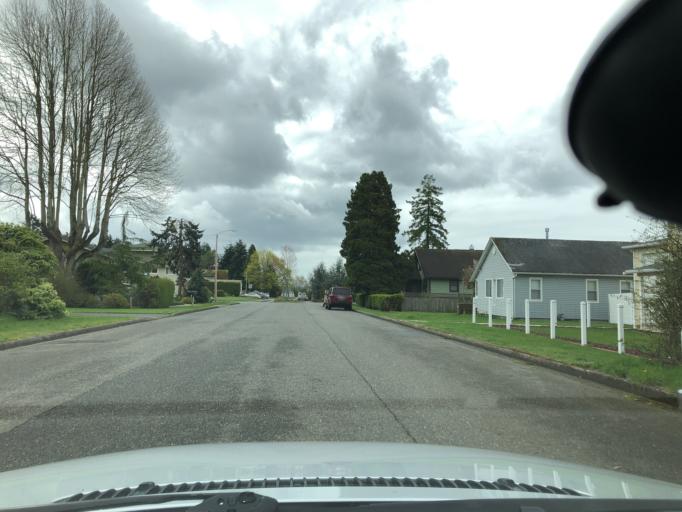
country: US
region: Washington
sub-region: Whatcom County
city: Blaine
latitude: 48.9884
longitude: -122.7481
